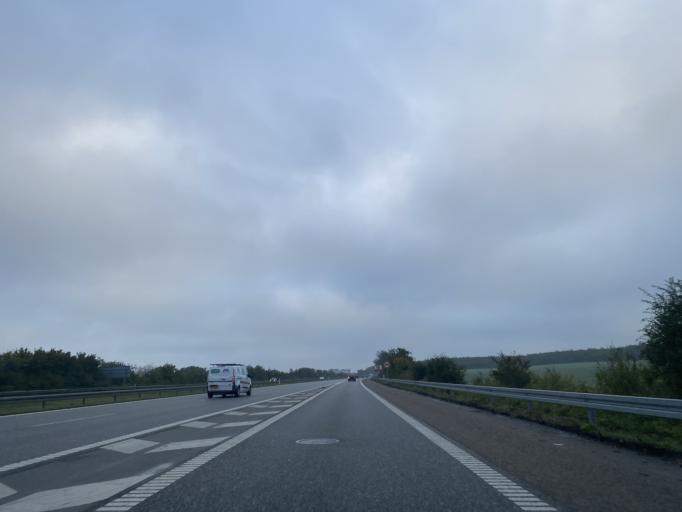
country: DK
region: Central Jutland
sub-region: Arhus Kommune
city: Kolt
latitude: 56.1105
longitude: 10.0572
